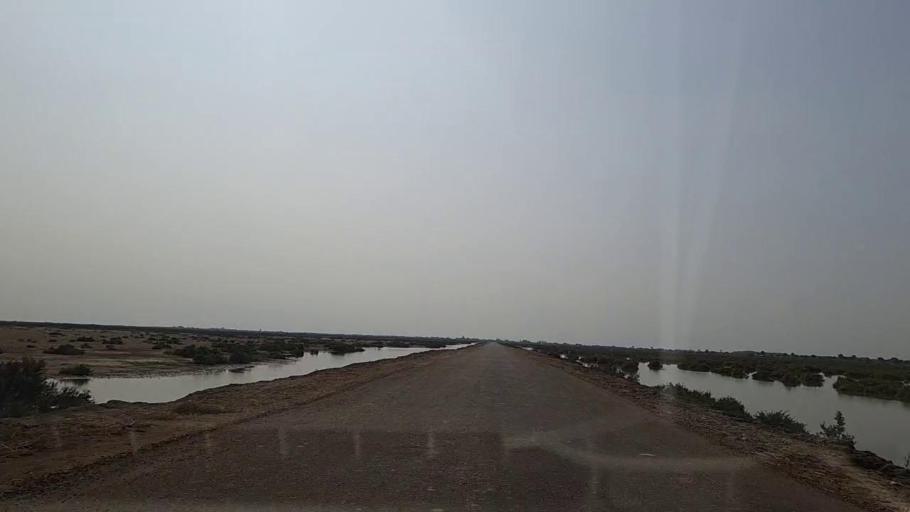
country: PK
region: Sindh
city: Chuhar Jamali
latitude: 24.2114
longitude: 67.8614
